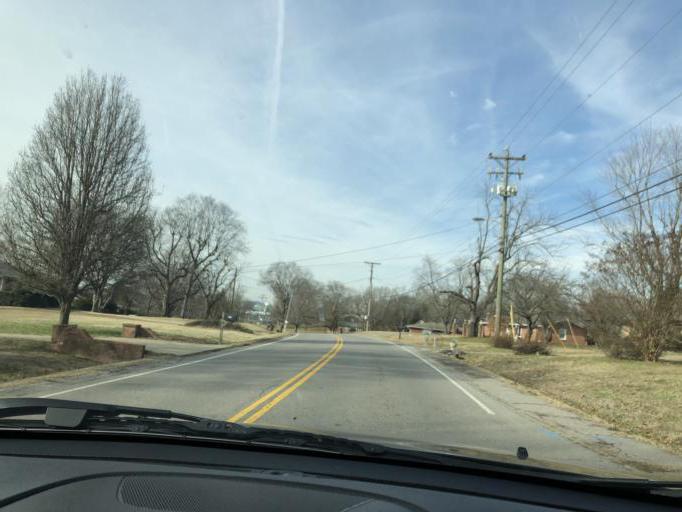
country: US
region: Tennessee
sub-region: Davidson County
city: Lakewood
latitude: 36.2085
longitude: -86.6818
